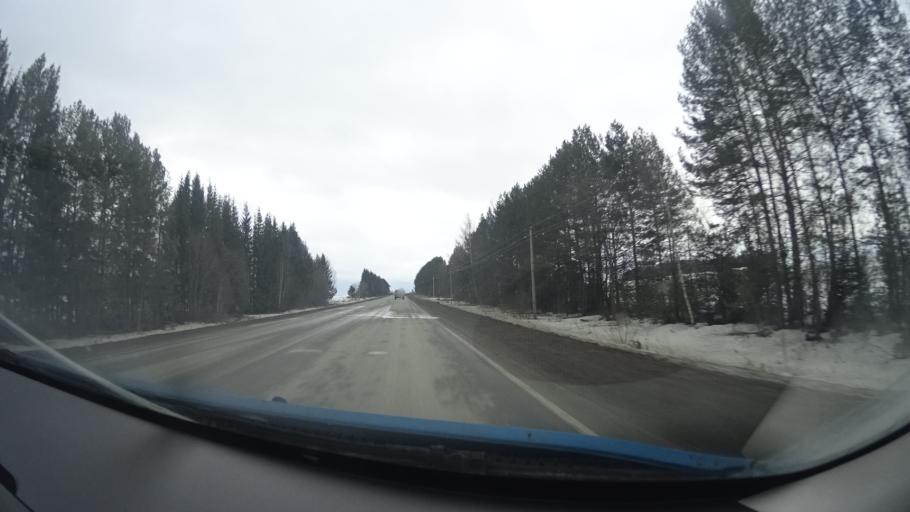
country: RU
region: Perm
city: Osa
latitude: 57.3205
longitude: 55.6177
